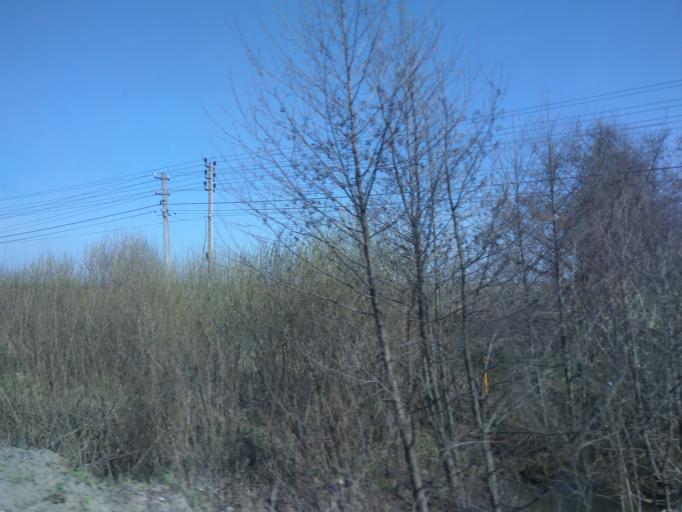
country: RU
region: Moskovskaya
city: Ramenskoye
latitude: 55.5778
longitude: 38.2802
